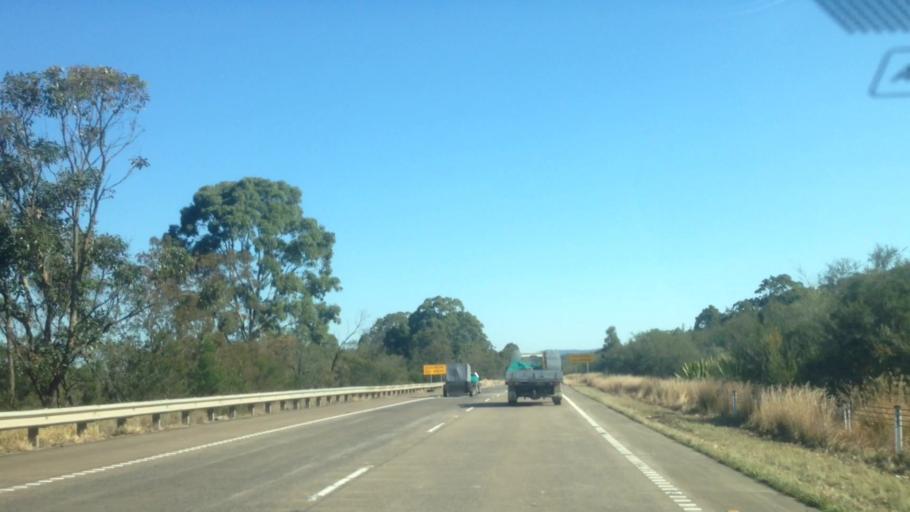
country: AU
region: New South Wales
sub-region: Wyong Shire
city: Charmhaven
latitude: -33.2026
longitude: 151.4604
